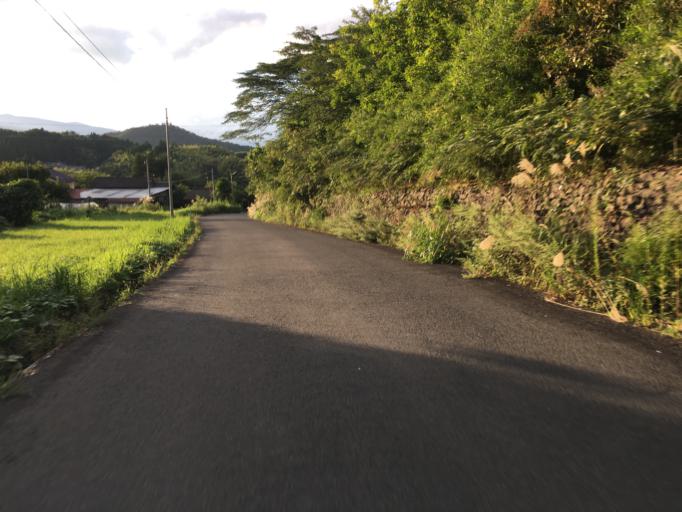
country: JP
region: Fukushima
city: Fukushima-shi
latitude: 37.6712
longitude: 140.4595
